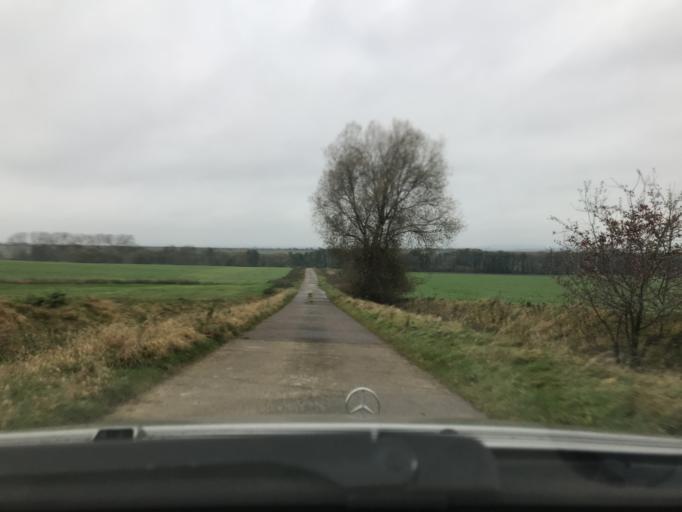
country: DE
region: Thuringia
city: Muehlhausen
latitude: 51.2380
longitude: 10.4126
